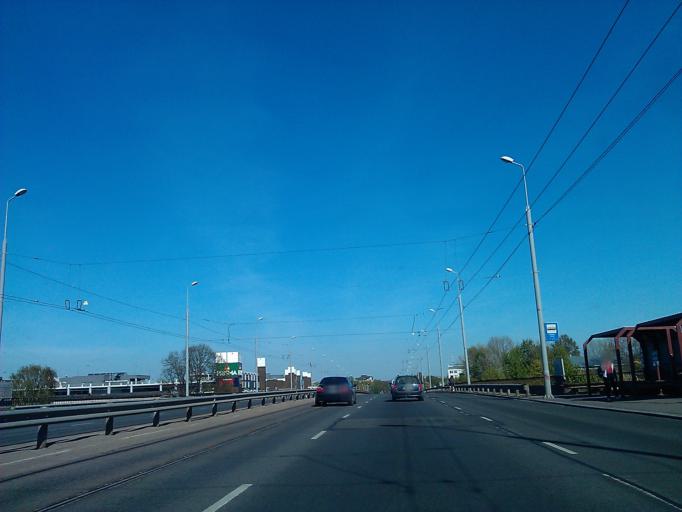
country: LV
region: Riga
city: Riga
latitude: 56.9648
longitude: 24.1559
